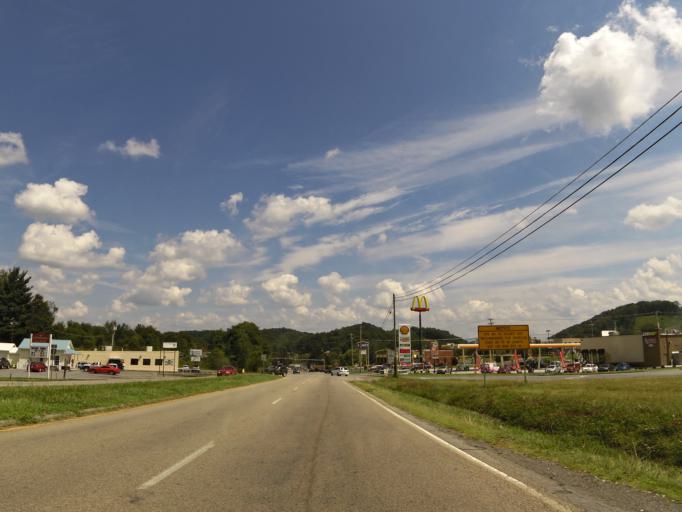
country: US
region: Virginia
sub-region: Washington County
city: Abingdon
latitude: 36.7133
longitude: -81.9326
